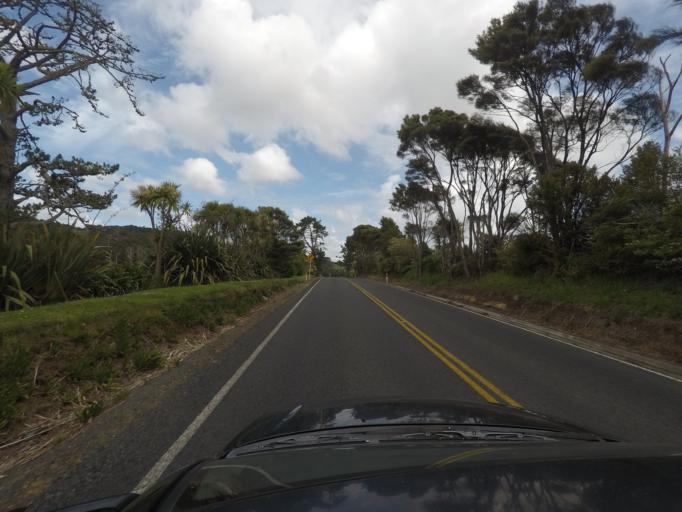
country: NZ
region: Auckland
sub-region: Auckland
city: Parakai
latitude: -36.6473
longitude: 174.5180
